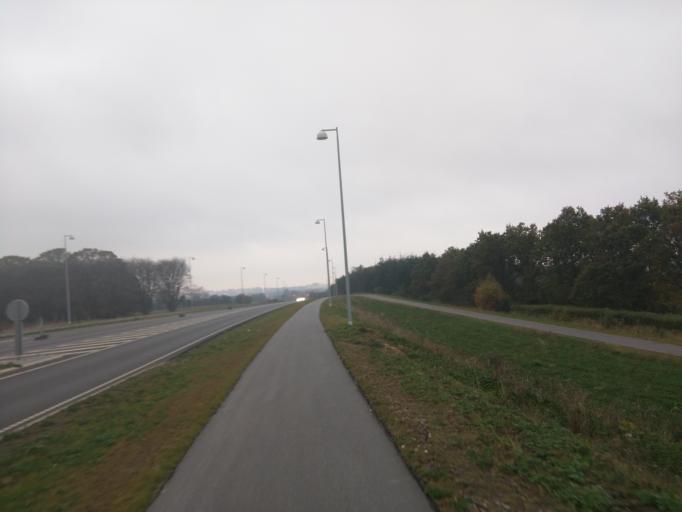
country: DK
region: Central Jutland
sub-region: Silkeborg Kommune
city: Silkeborg
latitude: 56.2036
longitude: 9.5123
